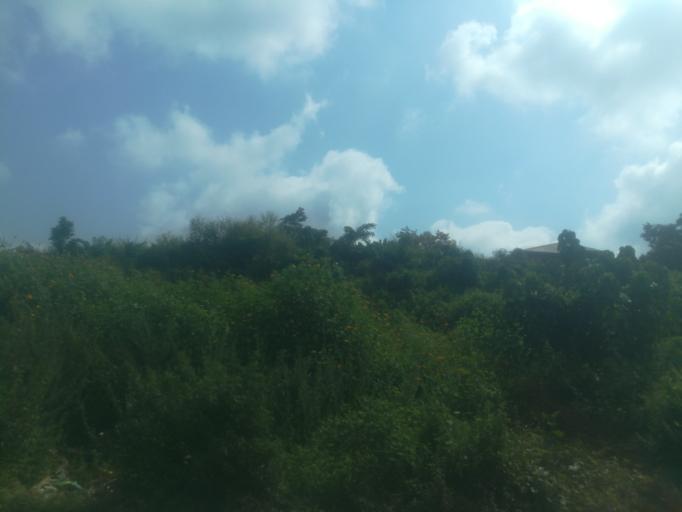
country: NG
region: Oyo
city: Moniya
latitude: 7.5332
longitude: 3.9167
